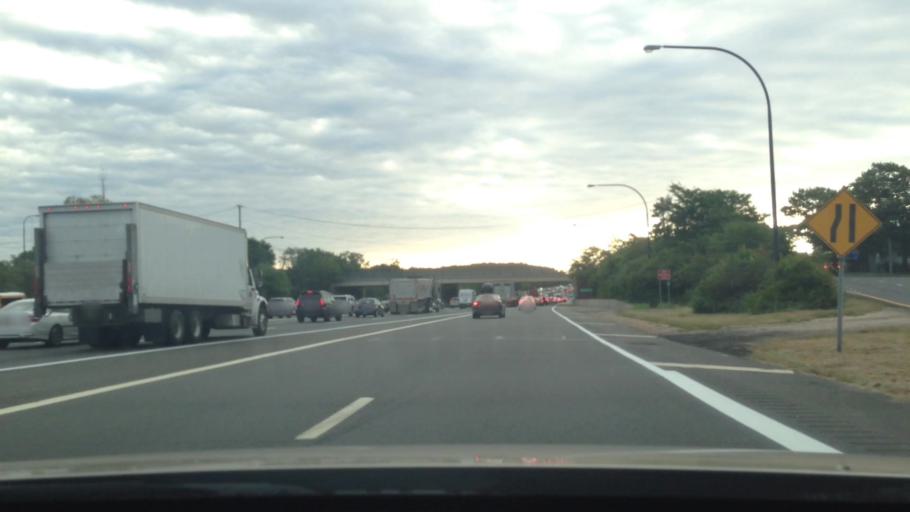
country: US
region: New York
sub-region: Nassau County
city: Plainview
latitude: 40.7961
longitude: -73.4704
